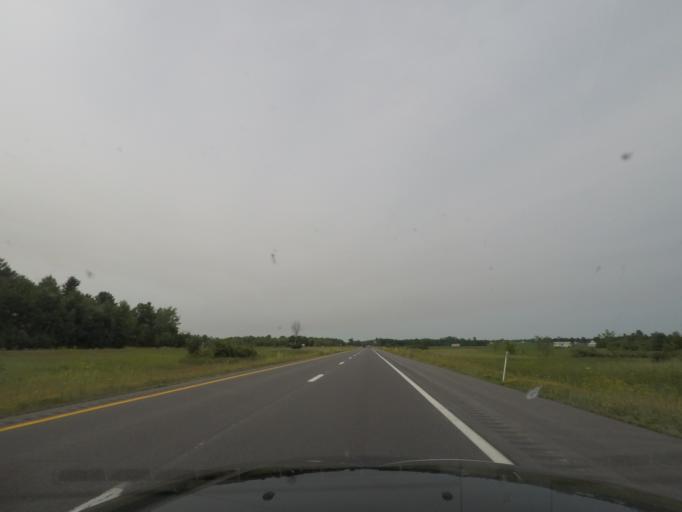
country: US
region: New York
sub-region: Clinton County
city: Cumberland Head
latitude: 44.8312
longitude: -73.4464
